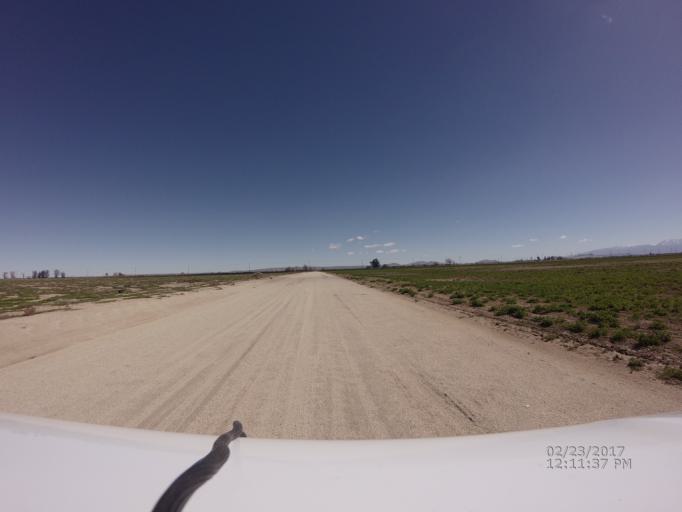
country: US
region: California
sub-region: Los Angeles County
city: Lancaster
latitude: 34.7414
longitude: -118.0094
